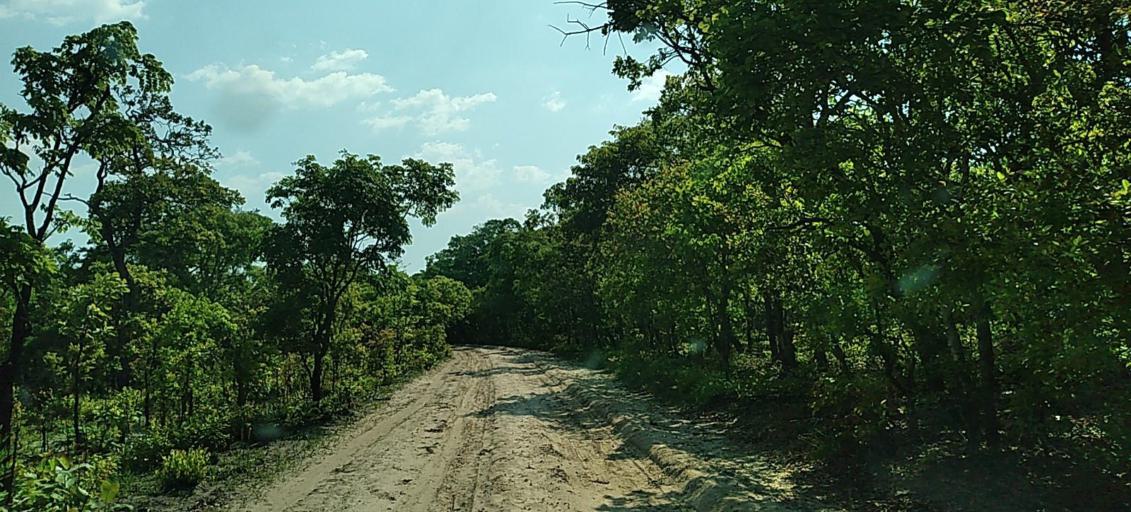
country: ZM
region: North-Western
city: Mwinilunga
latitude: -11.2775
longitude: 24.9281
